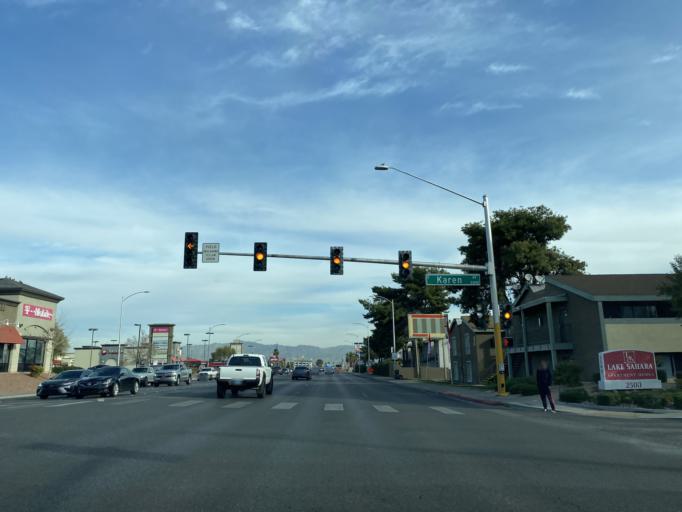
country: US
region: Nevada
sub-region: Clark County
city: Winchester
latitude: 36.1406
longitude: -115.1186
